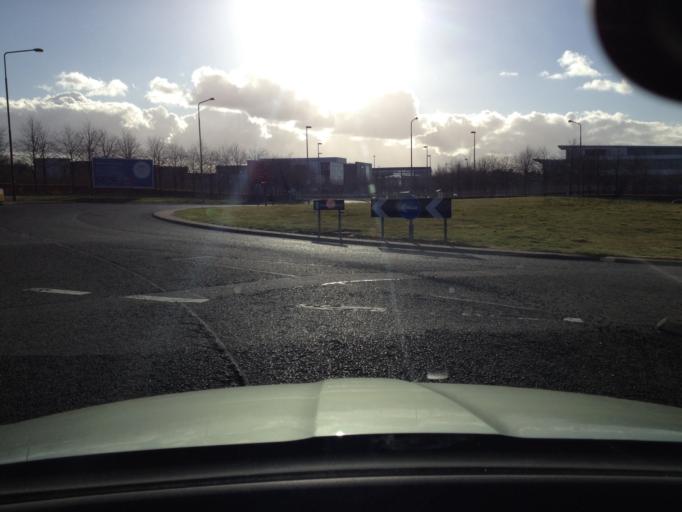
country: GB
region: Scotland
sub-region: West Lothian
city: Livingston
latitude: 55.8736
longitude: -3.5404
